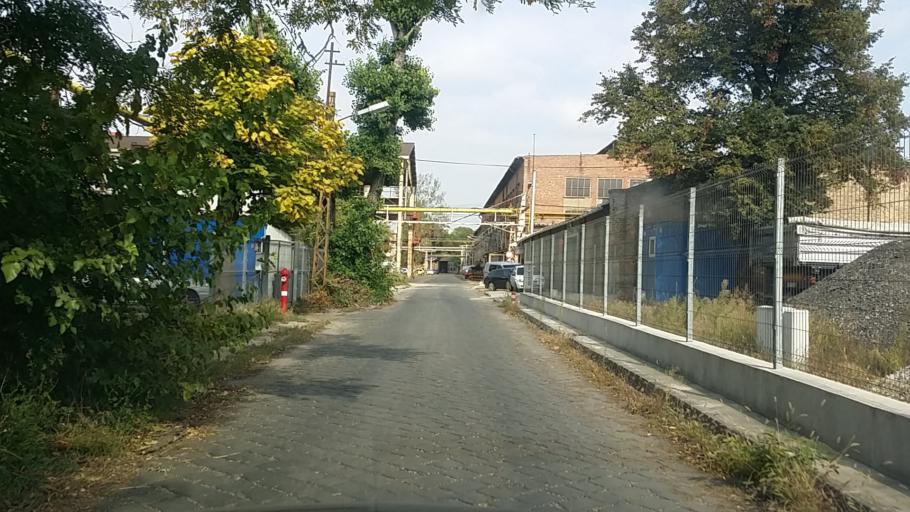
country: HU
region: Budapest
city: Budapest XXII. keruelet
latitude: 47.4244
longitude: 19.0519
